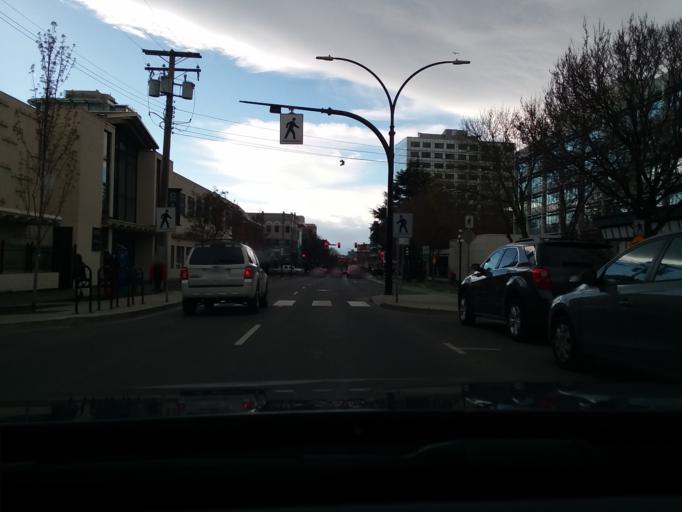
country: CA
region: British Columbia
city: Victoria
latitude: 48.4276
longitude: -123.3600
